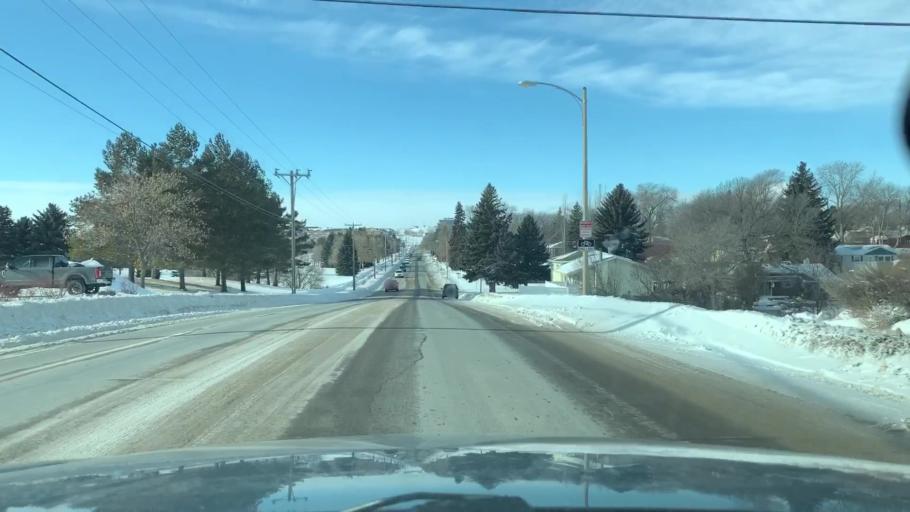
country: US
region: North Dakota
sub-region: Burleigh County
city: Bismarck
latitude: 46.8237
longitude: -100.7974
